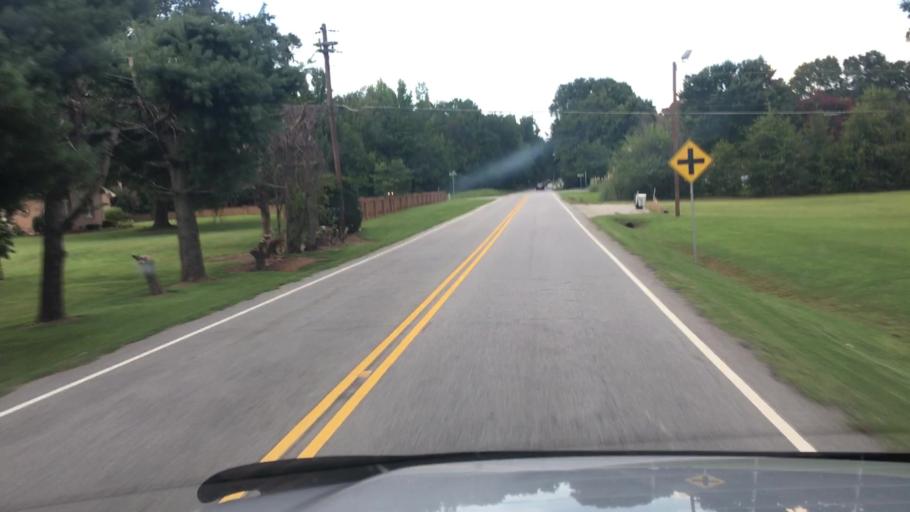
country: US
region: South Carolina
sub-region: Spartanburg County
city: Mayo
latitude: 35.1167
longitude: -81.8548
